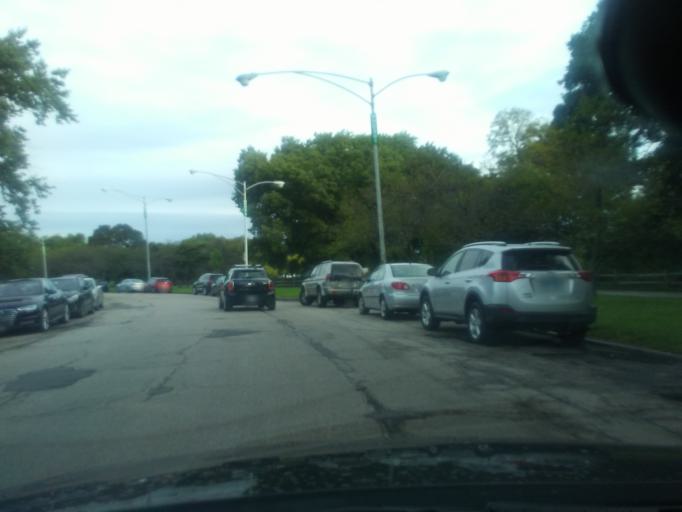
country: US
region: Illinois
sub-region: Cook County
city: Evanston
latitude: 41.9626
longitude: -87.6350
